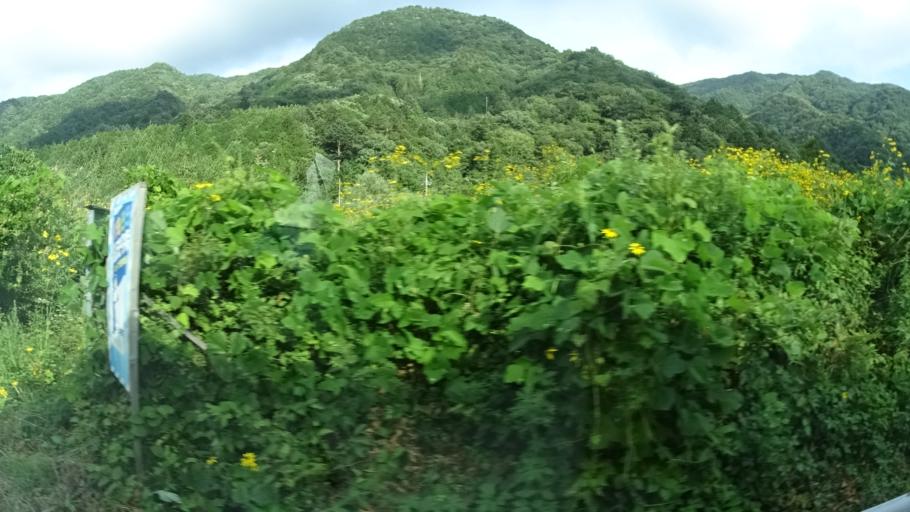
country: JP
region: Tochigi
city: Nikko
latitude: 36.6794
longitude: 139.4880
